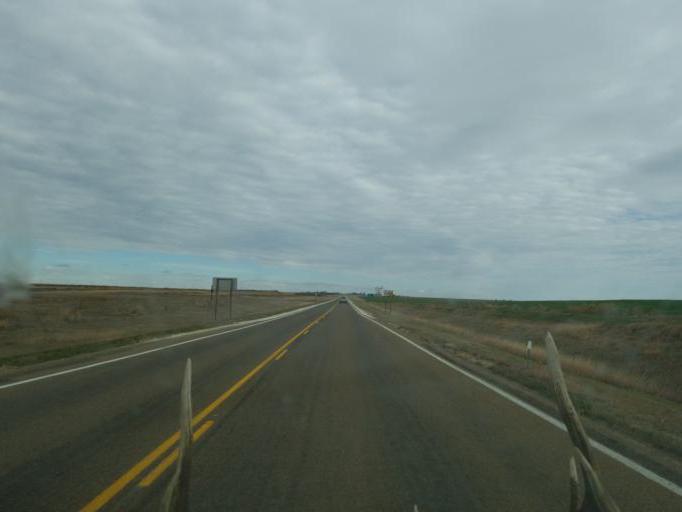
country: US
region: Kansas
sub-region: Logan County
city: Oakley
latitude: 39.0812
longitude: -101.1821
